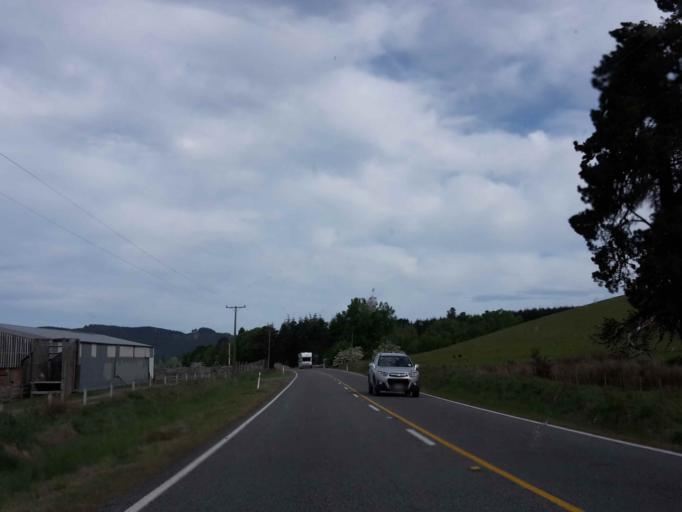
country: NZ
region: Canterbury
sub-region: Timaru District
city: Pleasant Point
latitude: -44.1075
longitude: 171.0086
